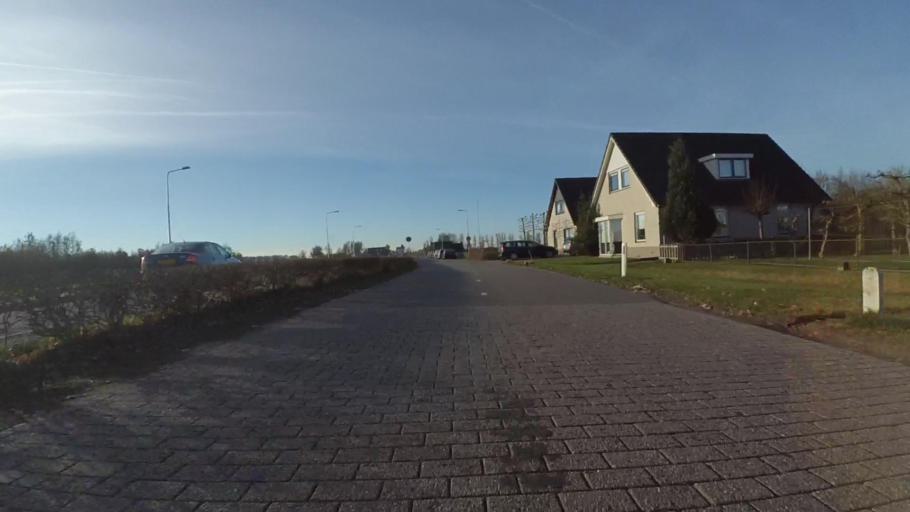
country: NL
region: Utrecht
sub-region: Gemeente Utrechtse Heuvelrug
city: Doorn
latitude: 52.0083
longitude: 5.3224
